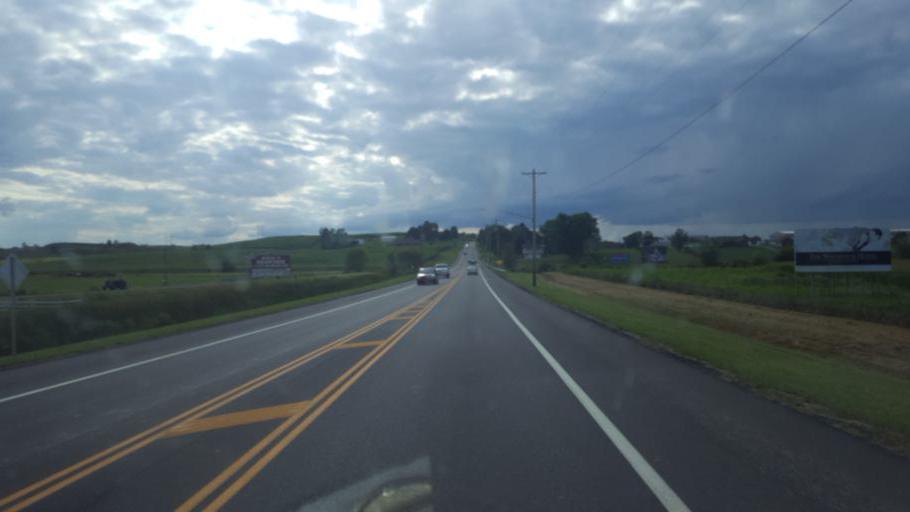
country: US
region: Ohio
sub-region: Tuscarawas County
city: Sugarcreek
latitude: 40.5095
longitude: -81.6121
